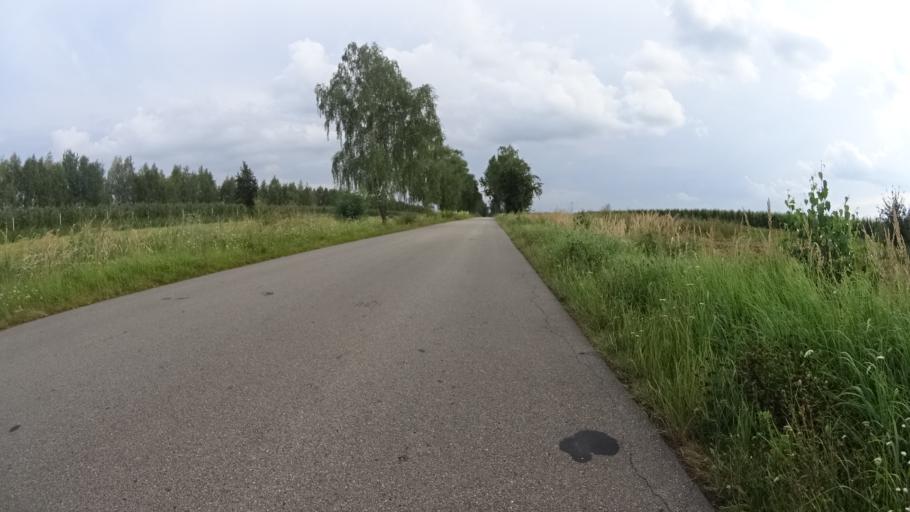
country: PL
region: Masovian Voivodeship
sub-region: Powiat grojecki
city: Goszczyn
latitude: 51.6971
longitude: 20.8561
